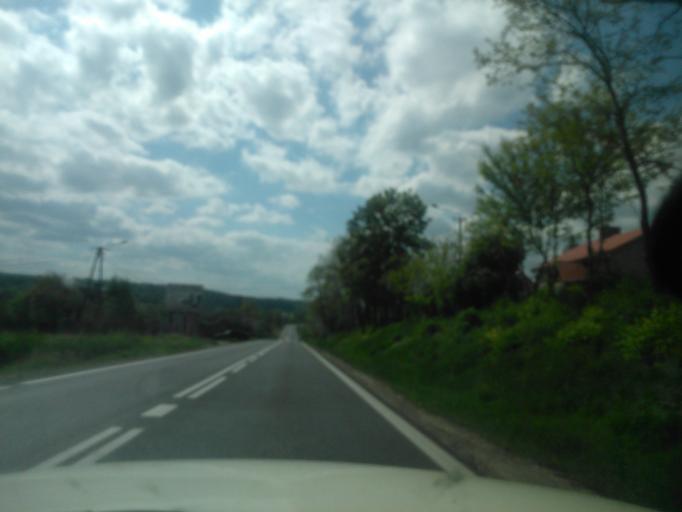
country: PL
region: Swietokrzyskie
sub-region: Powiat ostrowiecki
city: Kunow
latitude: 50.9491
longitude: 21.3091
